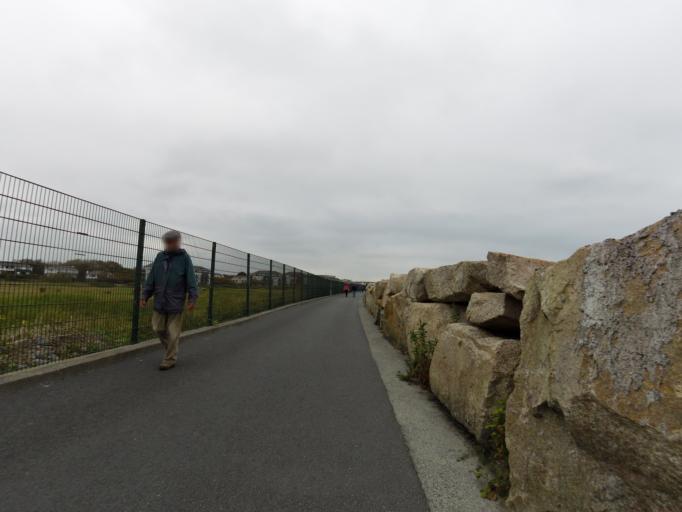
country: IE
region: Connaught
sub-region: County Galway
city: Gaillimh
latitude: 53.2562
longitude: -9.0966
